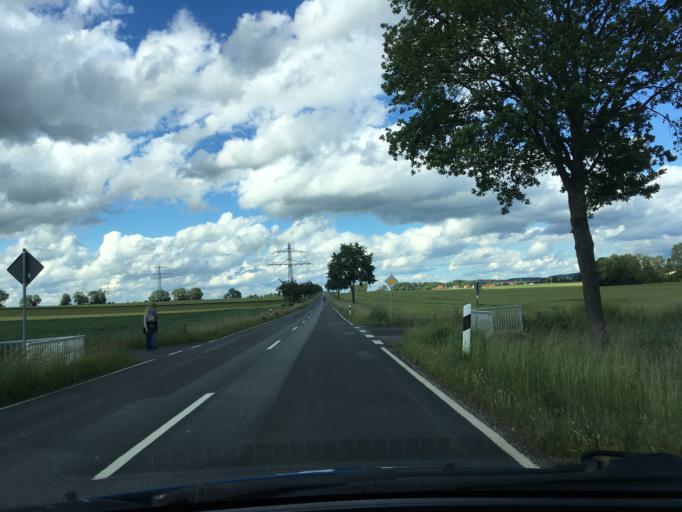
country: DE
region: Lower Saxony
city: Hardegsen
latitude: 51.6269
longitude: 9.8522
